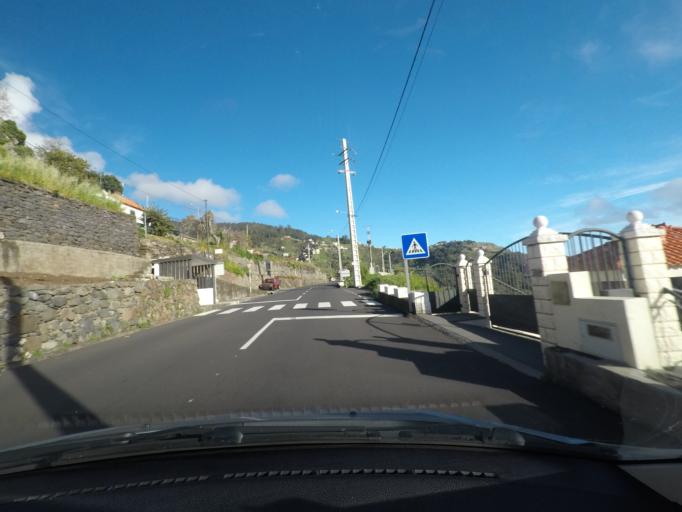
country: PT
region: Madeira
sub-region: Ribeira Brava
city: Campanario
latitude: 32.6686
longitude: -17.0348
